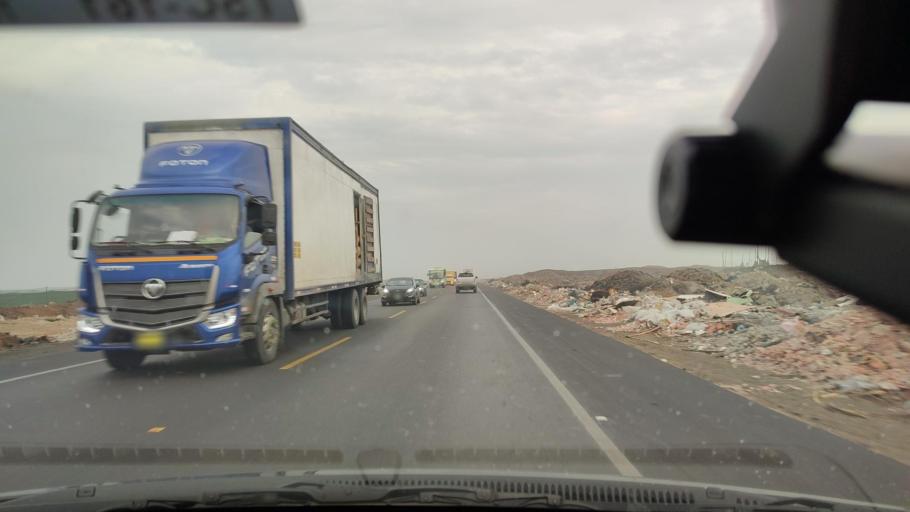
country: PE
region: La Libertad
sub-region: Provincia de Trujillo
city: Buenos Aires
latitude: -8.1265
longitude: -79.0757
